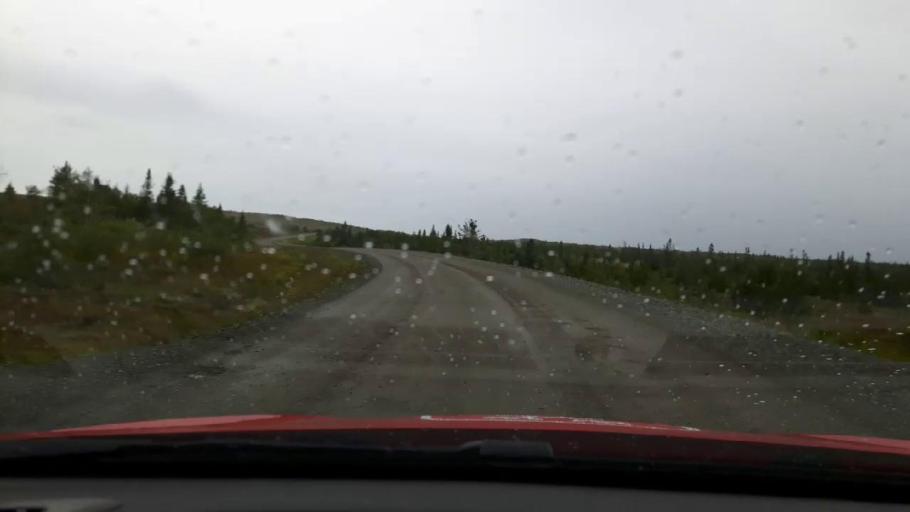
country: NO
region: Nord-Trondelag
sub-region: Meraker
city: Meraker
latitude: 63.6300
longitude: 12.2853
